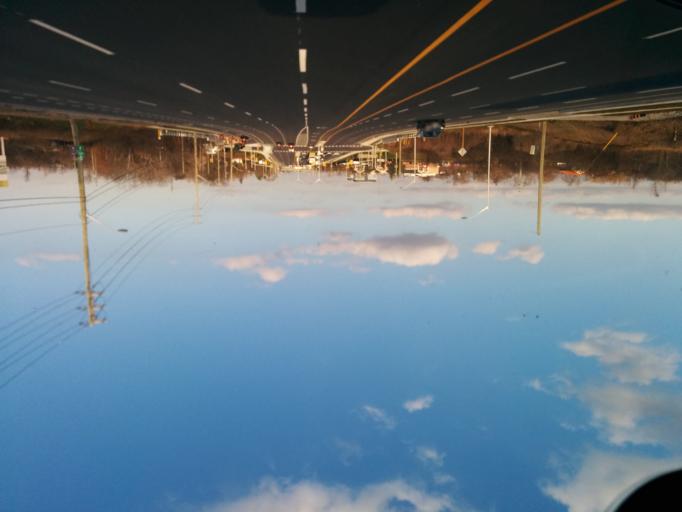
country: CA
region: Ontario
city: Oakville
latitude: 43.4935
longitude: -79.6813
